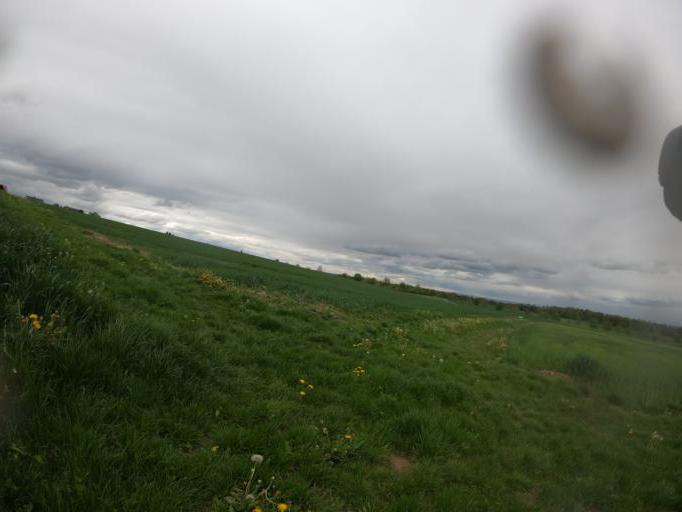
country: DE
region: Baden-Wuerttemberg
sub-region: Regierungsbezirk Stuttgart
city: Unterjettingen
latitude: 48.5579
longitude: 8.7789
